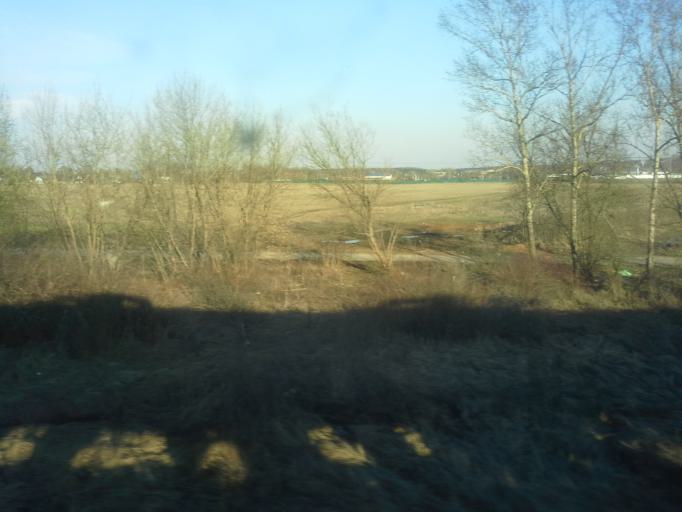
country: RU
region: Moskovskaya
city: Nekrasovskiy
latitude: 56.0823
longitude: 37.5001
